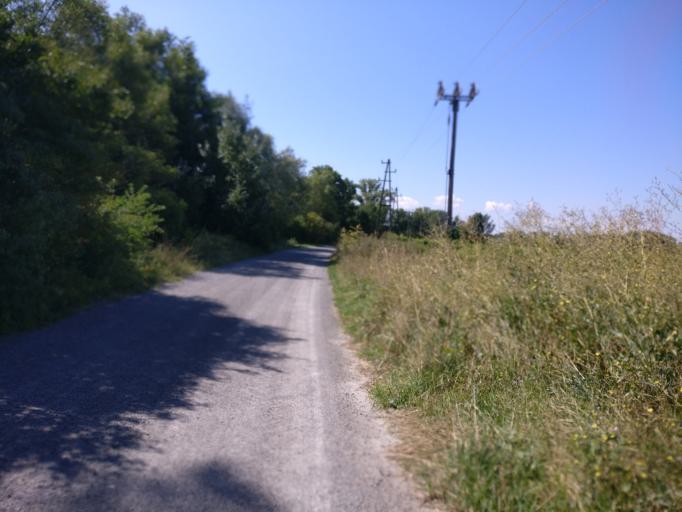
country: AT
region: Lower Austria
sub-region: Politischer Bezirk Baden
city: Pottendorf
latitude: 47.9105
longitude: 16.3544
